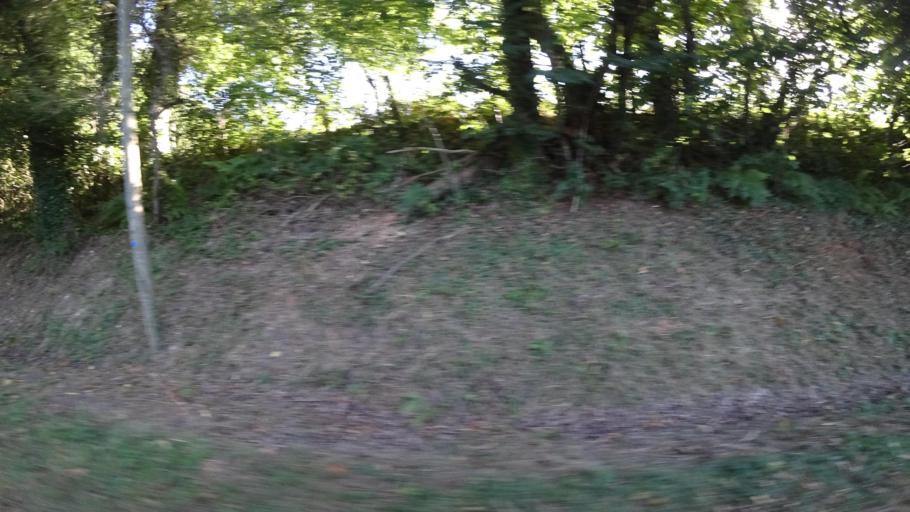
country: FR
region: Midi-Pyrenees
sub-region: Departement de l'Aveyron
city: Cransac
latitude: 44.5220
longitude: 2.3018
